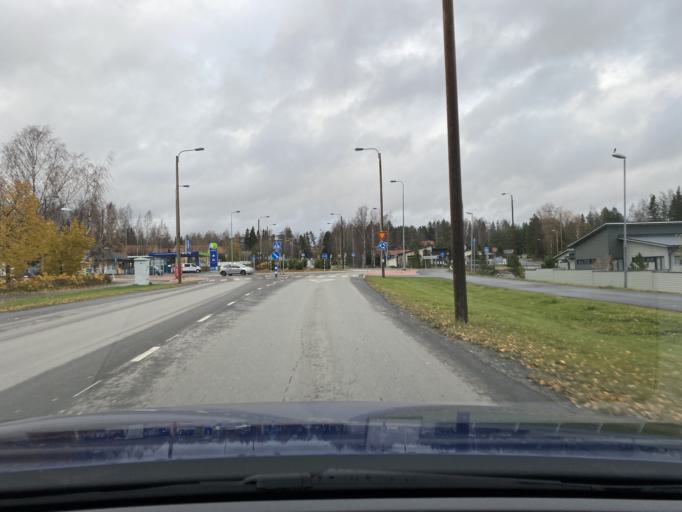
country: FI
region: Pirkanmaa
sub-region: Tampere
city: Lempaeaelae
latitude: 61.3314
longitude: 23.7496
